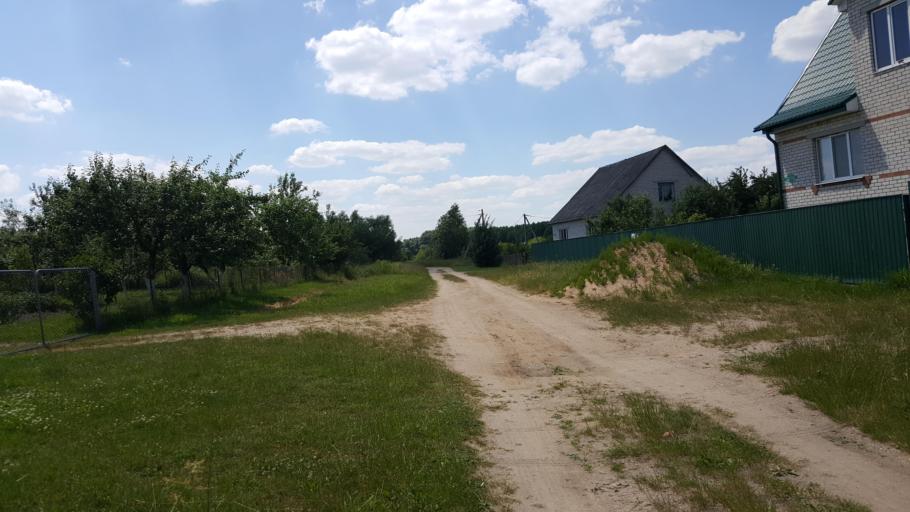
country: BY
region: Brest
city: Kamyanyets
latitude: 52.4115
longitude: 23.8316
